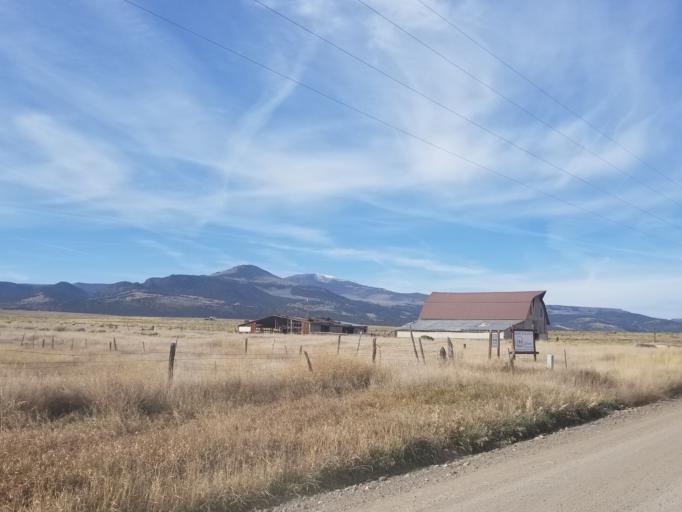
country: US
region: Colorado
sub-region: Rio Grande County
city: Del Norte
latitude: 37.6622
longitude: -106.4328
